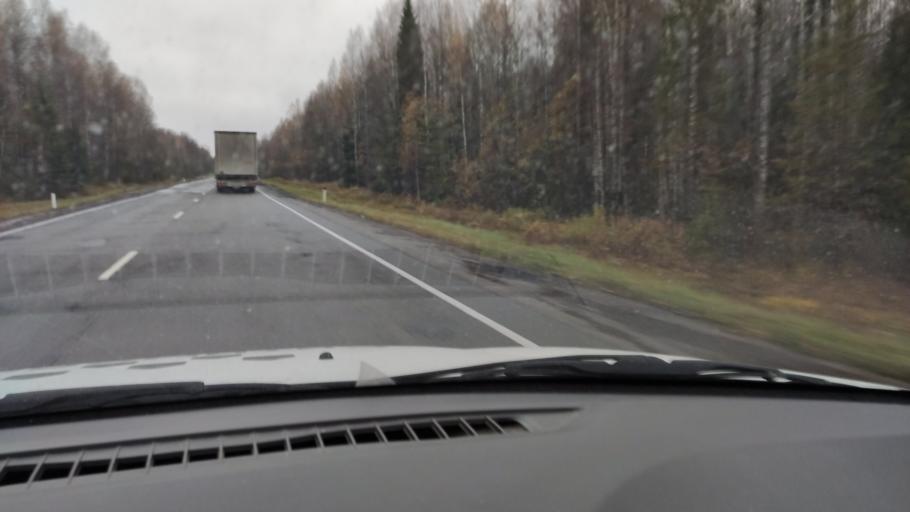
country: RU
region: Kirov
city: Omutninsk
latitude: 58.7662
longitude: 51.9803
